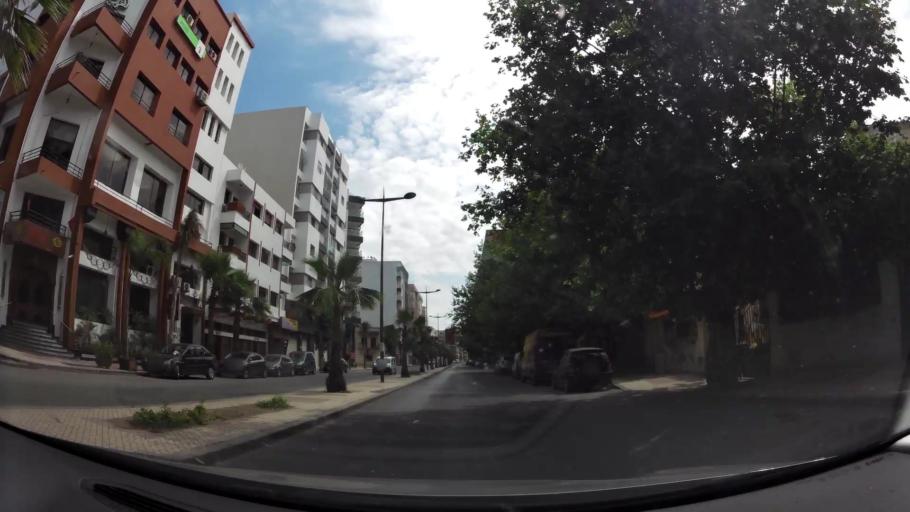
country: MA
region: Gharb-Chrarda-Beni Hssen
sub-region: Kenitra Province
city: Kenitra
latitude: 34.2603
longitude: -6.5880
